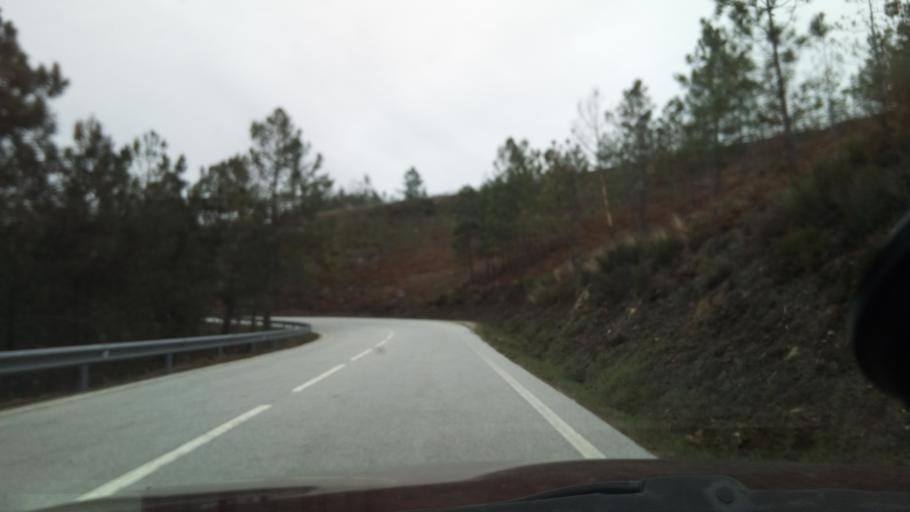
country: PT
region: Guarda
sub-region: Seia
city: Seia
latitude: 40.3398
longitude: -7.7128
